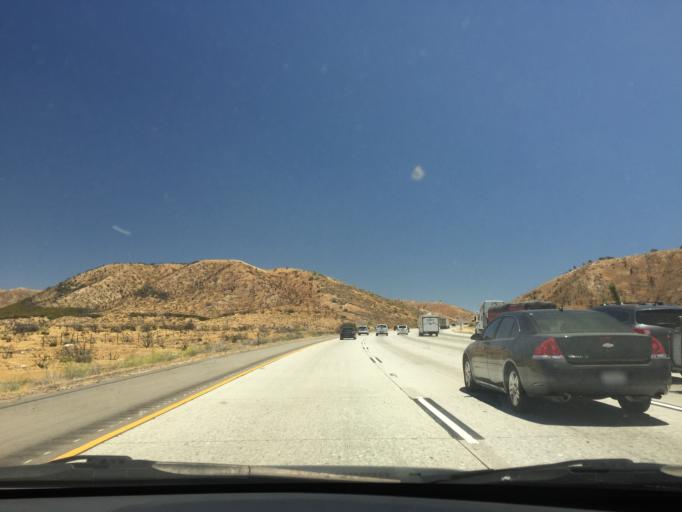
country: US
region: California
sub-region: San Bernardino County
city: Oak Hills
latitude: 34.3399
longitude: -117.4752
